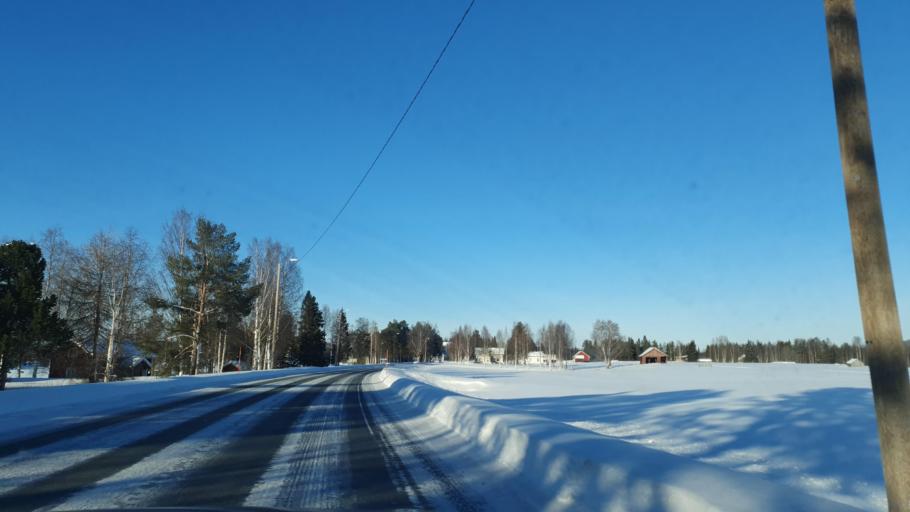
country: FI
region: Lapland
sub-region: Torniolaakso
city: Pello
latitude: 66.6478
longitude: 23.8768
